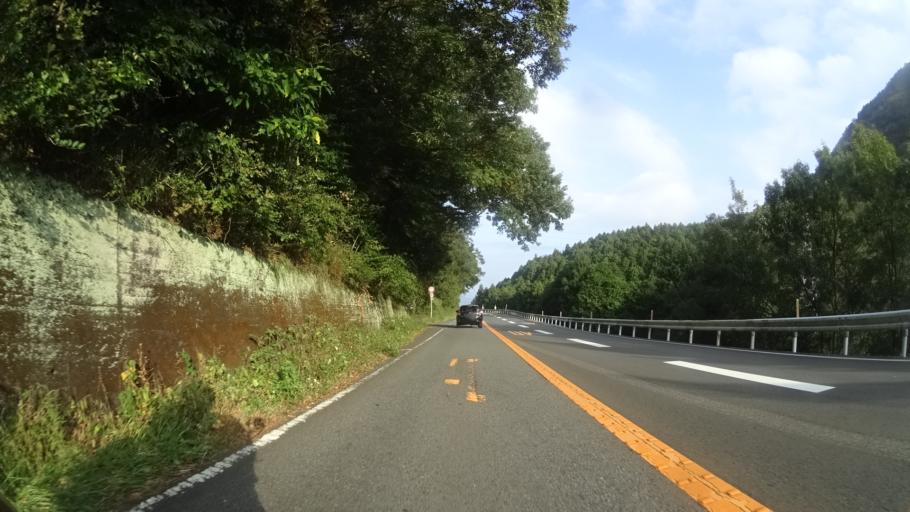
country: JP
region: Oita
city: Beppu
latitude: 33.2849
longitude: 131.4556
